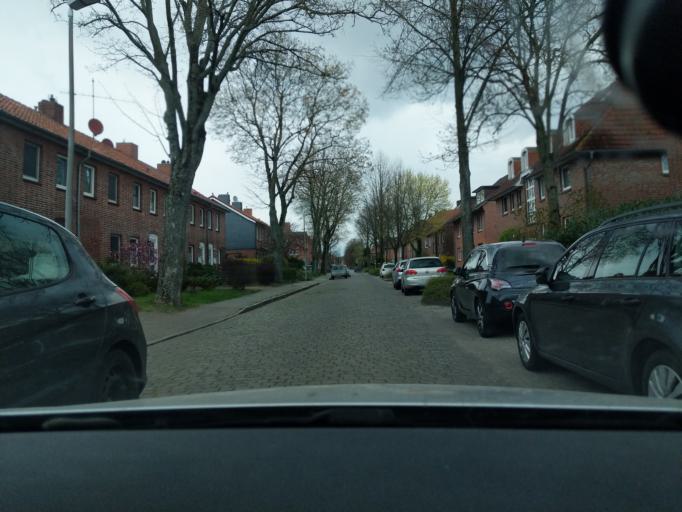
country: DE
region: Lower Saxony
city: Stade
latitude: 53.5900
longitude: 9.4651
